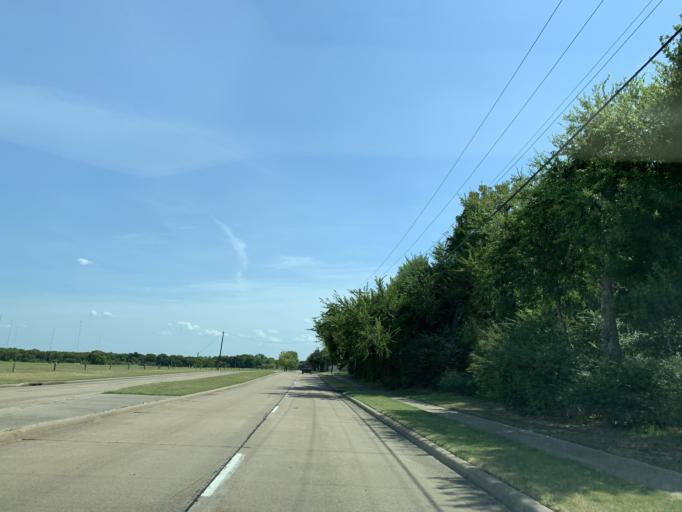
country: US
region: Texas
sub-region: Dallas County
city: Cedar Hill
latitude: 32.6485
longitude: -97.0146
